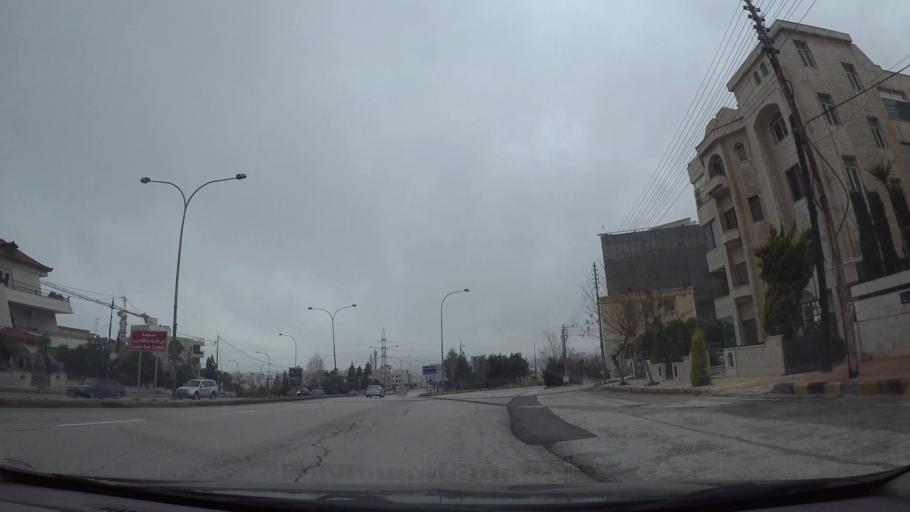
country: JO
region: Amman
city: Wadi as Sir
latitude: 31.9457
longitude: 35.8609
